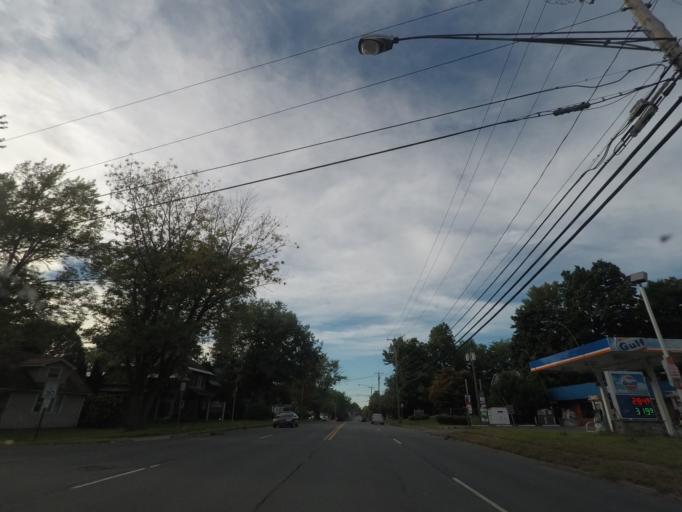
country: US
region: New York
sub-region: Rensselaer County
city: East Greenbush
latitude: 42.5848
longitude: -73.6951
